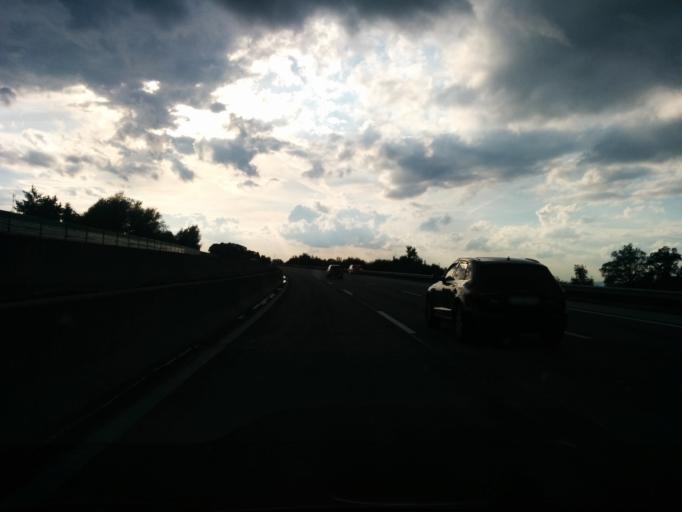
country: AT
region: Lower Austria
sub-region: Politischer Bezirk Amstetten
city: Strengberg
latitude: 48.1184
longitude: 14.6495
